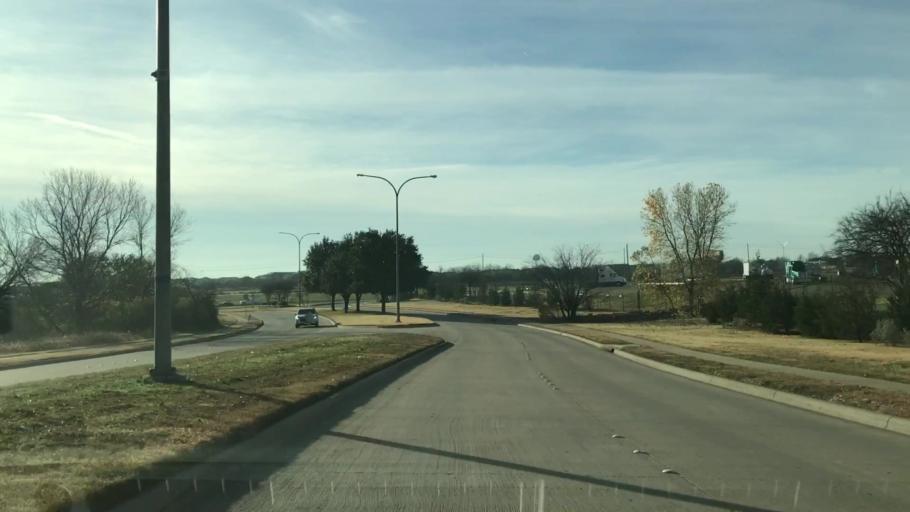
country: US
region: Texas
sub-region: Tarrant County
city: Sansom Park
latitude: 32.8197
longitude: -97.4054
